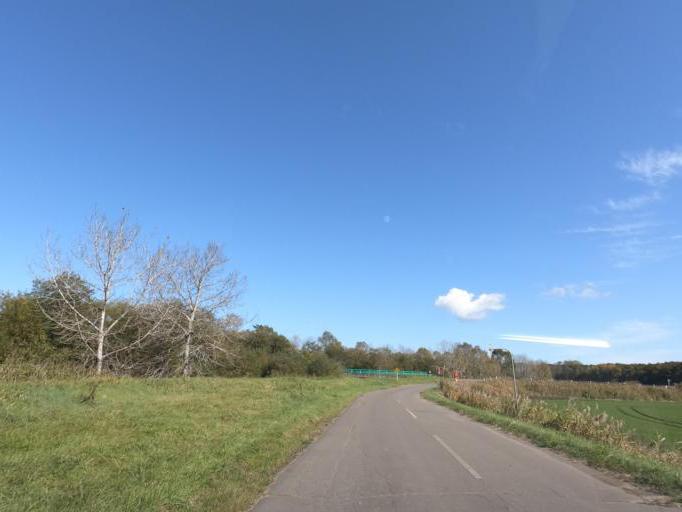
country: JP
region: Hokkaido
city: Otofuke
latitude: 43.0586
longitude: 143.2785
